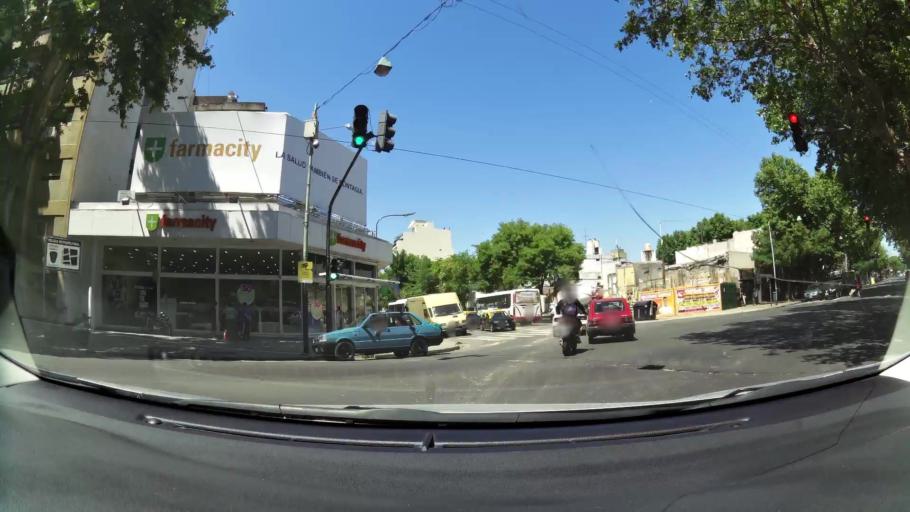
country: AR
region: Buenos Aires F.D.
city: Buenos Aires
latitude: -34.6388
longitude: -58.4159
